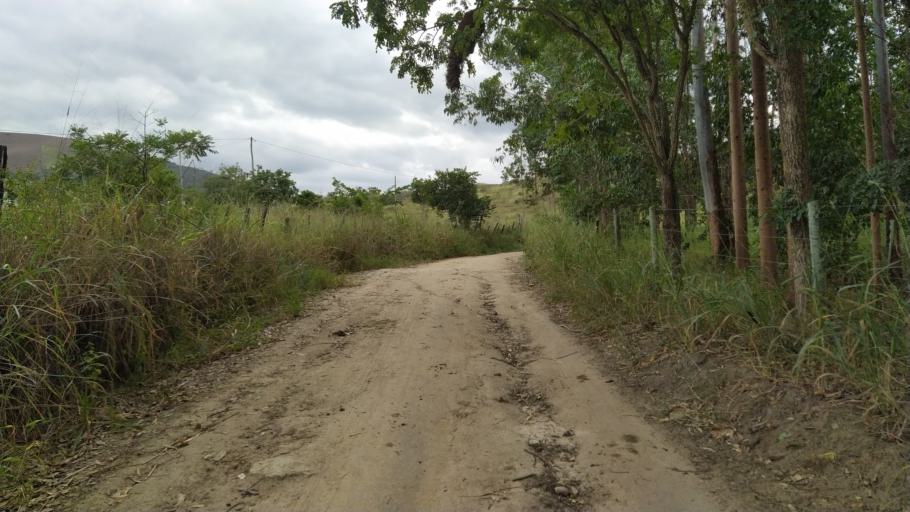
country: BR
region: Minas Gerais
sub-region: Almenara
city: Almenara
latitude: -16.6295
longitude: -40.4570
